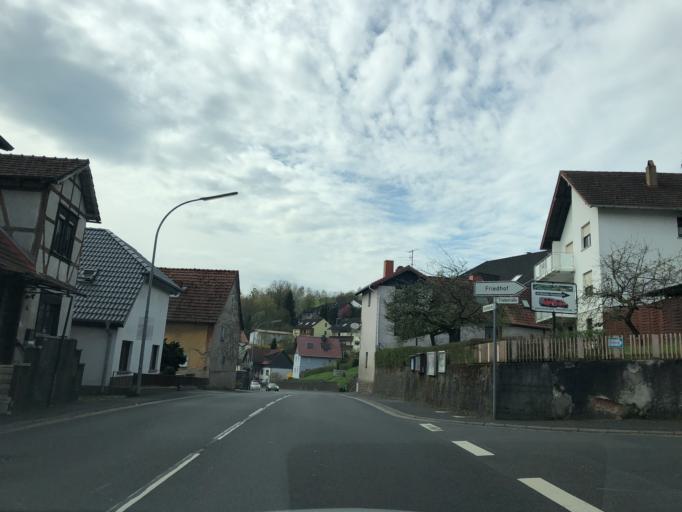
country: DE
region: Hesse
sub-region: Regierungsbezirk Darmstadt
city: Wachtersbach
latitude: 50.2730
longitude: 9.3065
